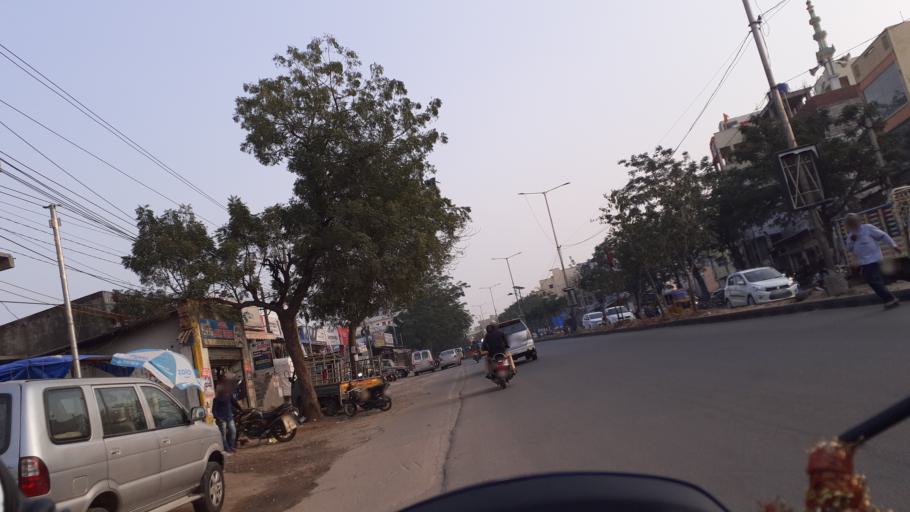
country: IN
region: Telangana
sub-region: Rangareddi
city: Kukatpalli
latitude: 17.4789
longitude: 78.3616
